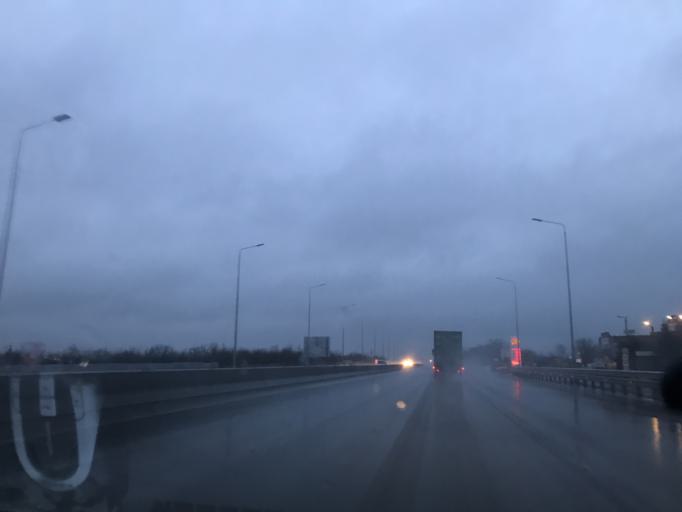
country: RU
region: Rostov
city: Samarskoye
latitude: 46.9383
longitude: 39.7105
